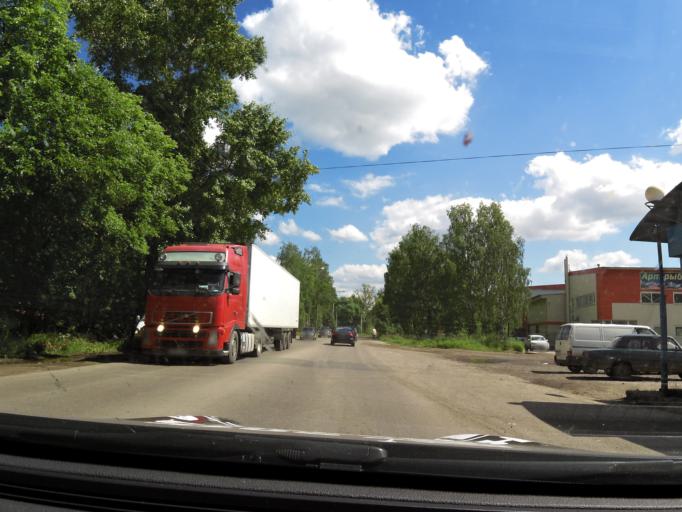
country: RU
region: Vologda
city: Vologda
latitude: 59.2384
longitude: 39.8098
